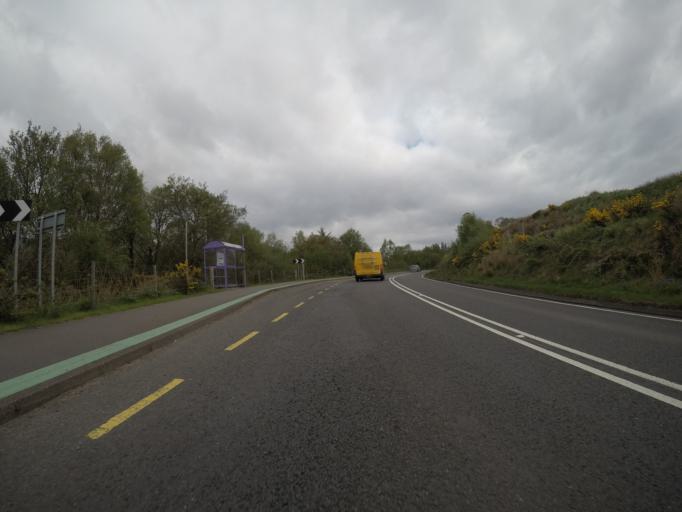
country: GB
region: Scotland
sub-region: Highland
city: Fort William
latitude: 56.7179
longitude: -5.2326
